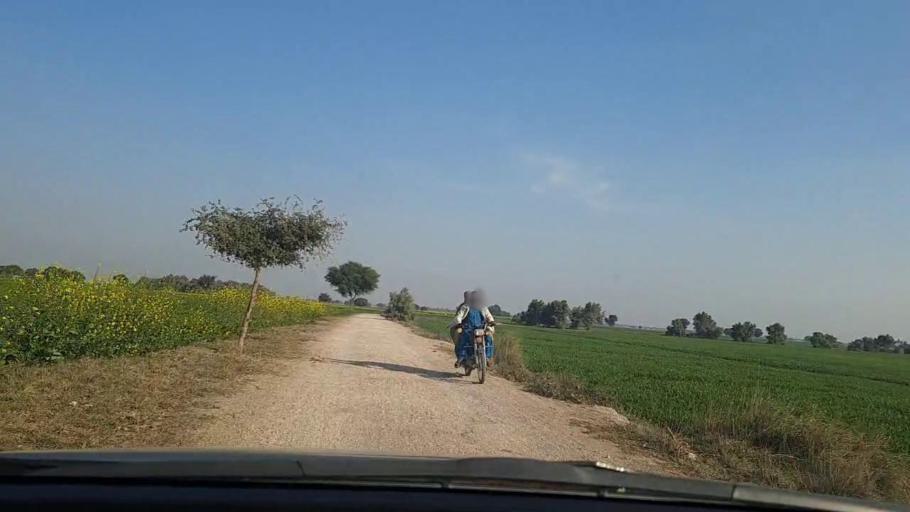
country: PK
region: Sindh
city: Sehwan
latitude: 26.3044
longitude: 68.0030
